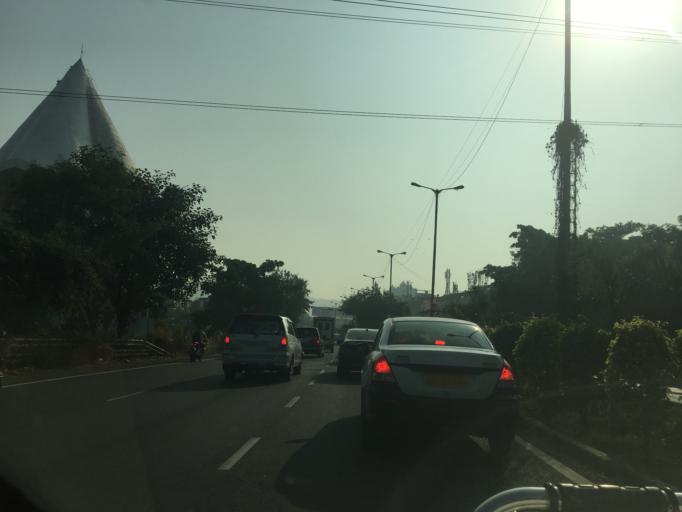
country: IN
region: Maharashtra
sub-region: Thane
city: Airoli
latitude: 19.1493
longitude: 72.9888
